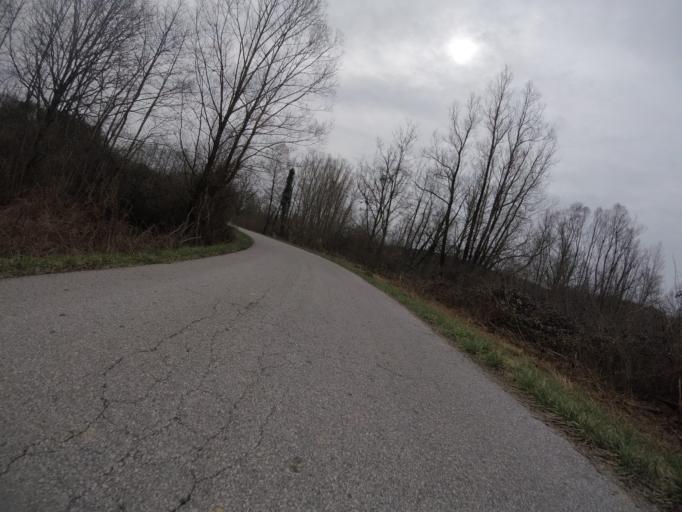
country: HR
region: Zagrebacka
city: Lukavec
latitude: 45.5664
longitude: 15.9653
